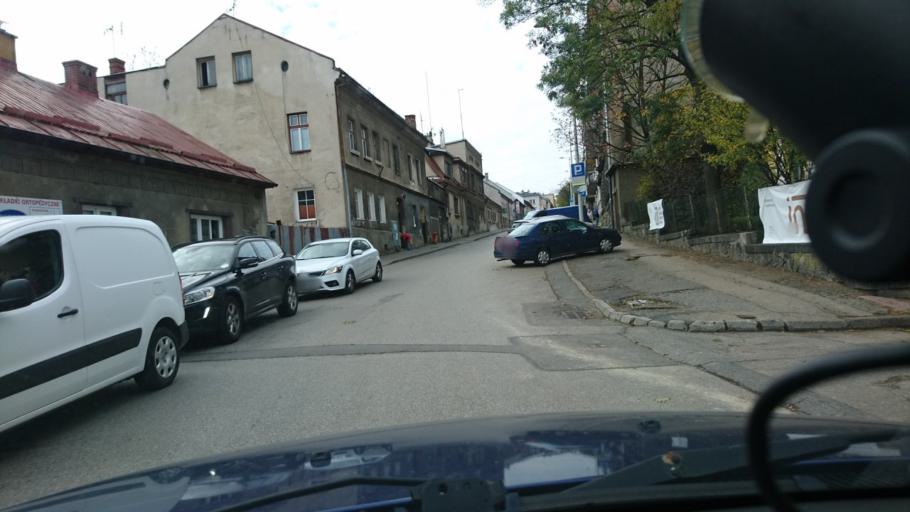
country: PL
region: Silesian Voivodeship
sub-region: Bielsko-Biala
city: Bielsko-Biala
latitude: 49.8192
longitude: 19.0404
